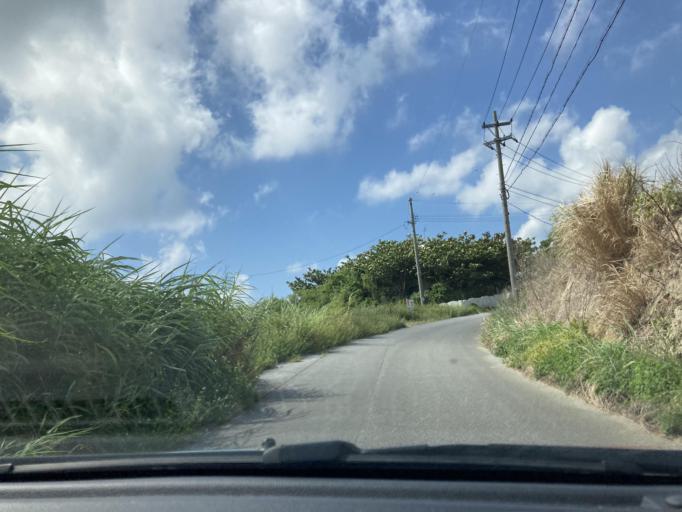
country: JP
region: Okinawa
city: Itoman
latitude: 26.1001
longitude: 127.7306
